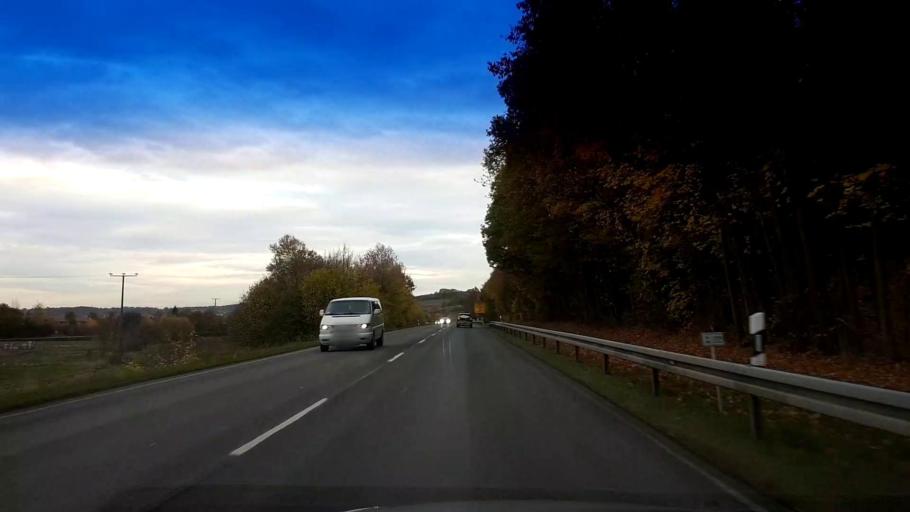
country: DE
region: Bavaria
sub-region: Regierungsbezirk Unterfranken
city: Stettfeld
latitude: 49.9400
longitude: 10.7302
